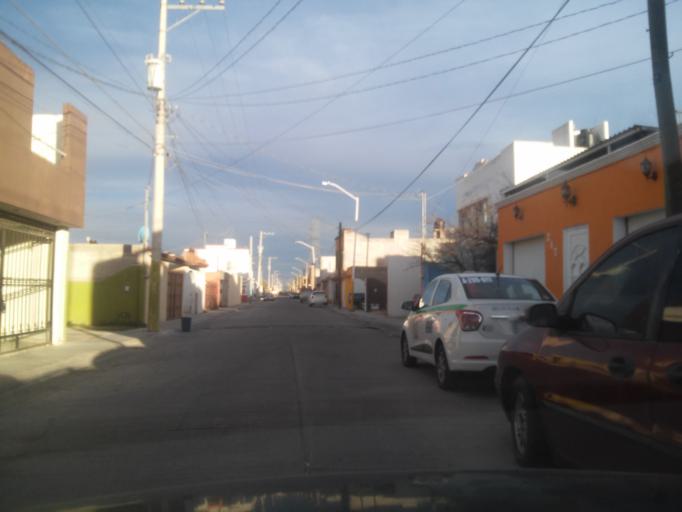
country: MX
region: Durango
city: Victoria de Durango
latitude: 24.0033
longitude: -104.6340
